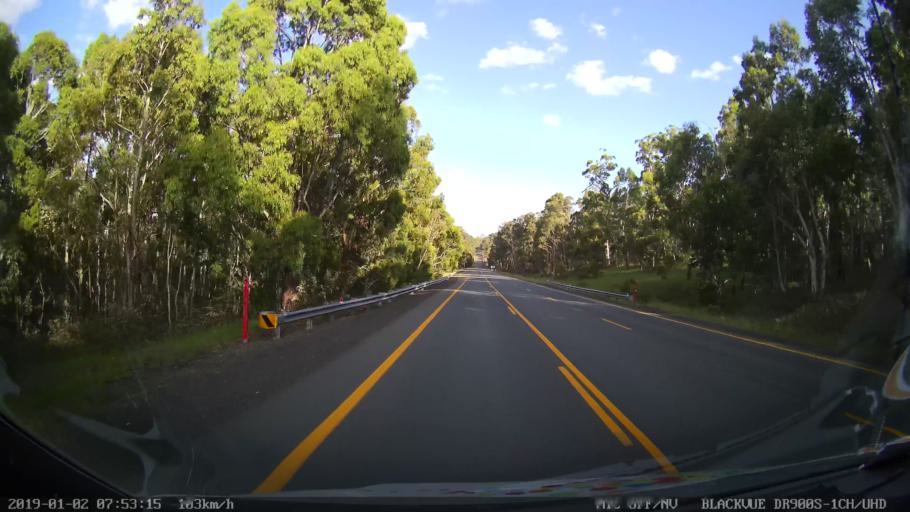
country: AU
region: New South Wales
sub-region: Tumut Shire
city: Tumut
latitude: -35.7075
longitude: 148.5087
